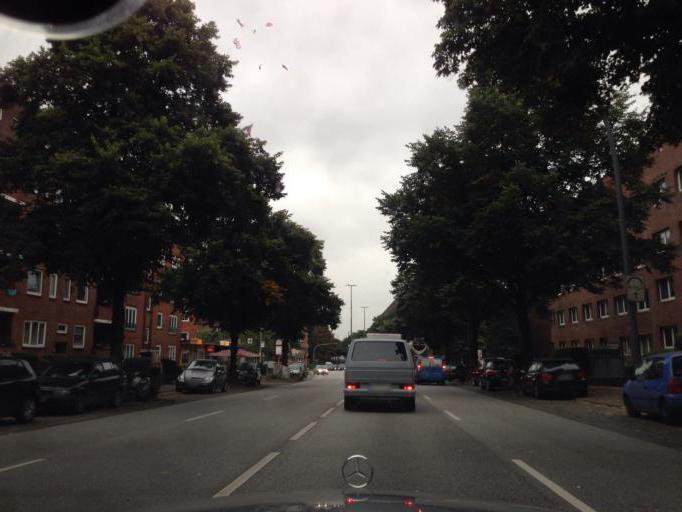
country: DE
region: Hamburg
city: Barmbek-Nord
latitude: 53.5950
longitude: 10.0484
